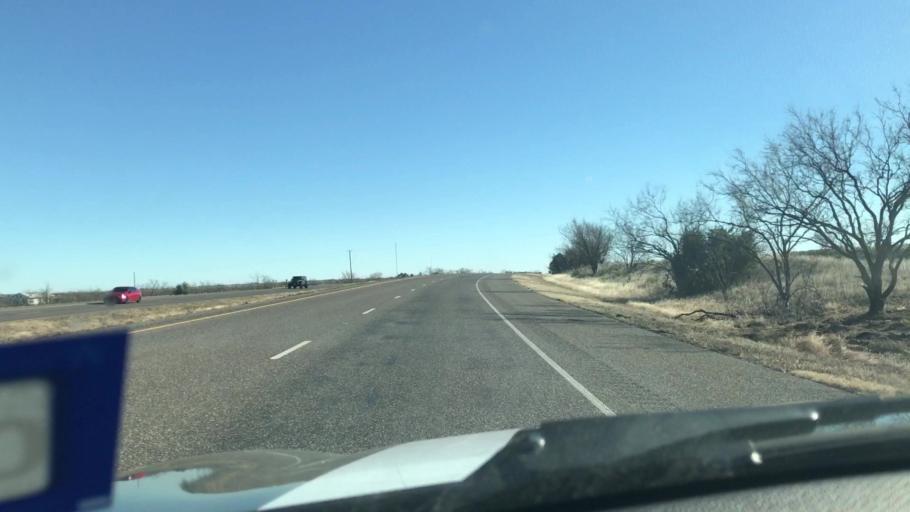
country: US
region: Texas
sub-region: Scurry County
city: Snyder
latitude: 32.8328
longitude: -100.9870
